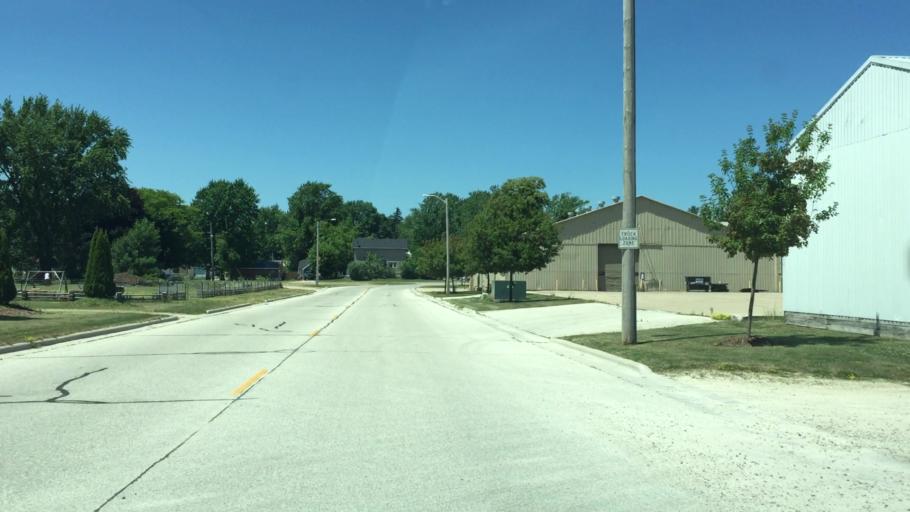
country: US
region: Wisconsin
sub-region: Calumet County
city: New Holstein
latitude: 43.9485
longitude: -88.0861
